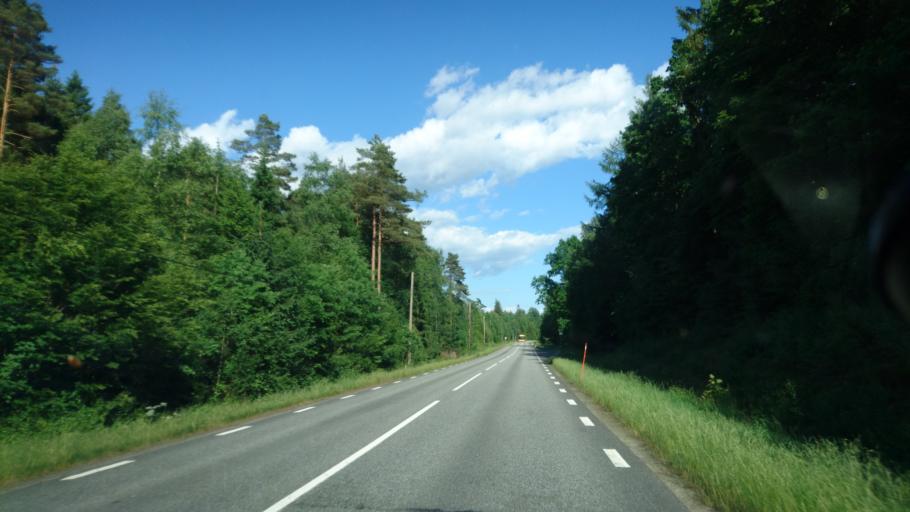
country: SE
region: Kronoberg
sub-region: Almhults Kommun
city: AElmhult
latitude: 56.4809
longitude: 14.1986
